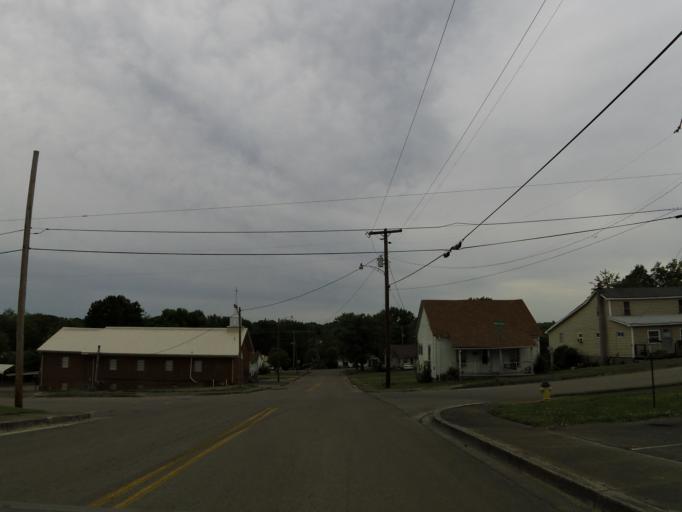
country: US
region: Tennessee
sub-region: Blount County
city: Alcoa
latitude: 35.7759
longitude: -83.9573
